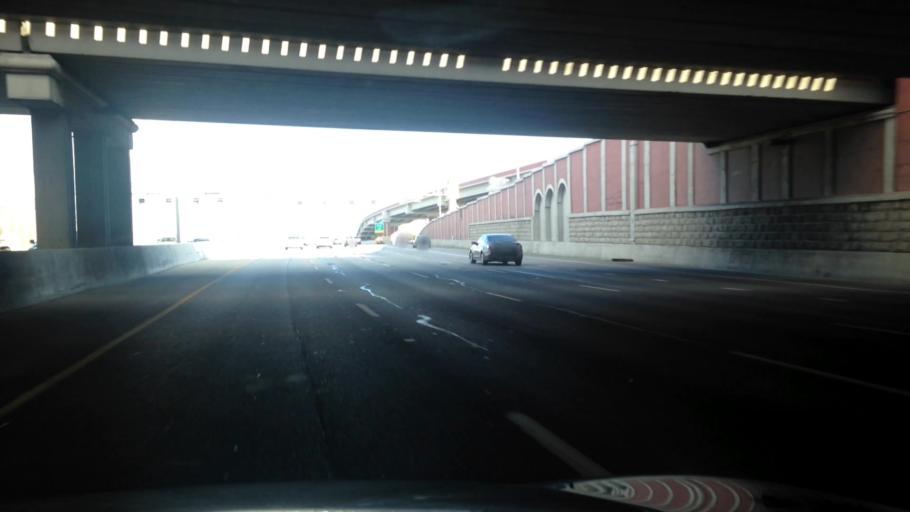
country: US
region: Texas
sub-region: Bexar County
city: Alamo Heights
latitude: 29.5199
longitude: -98.4770
